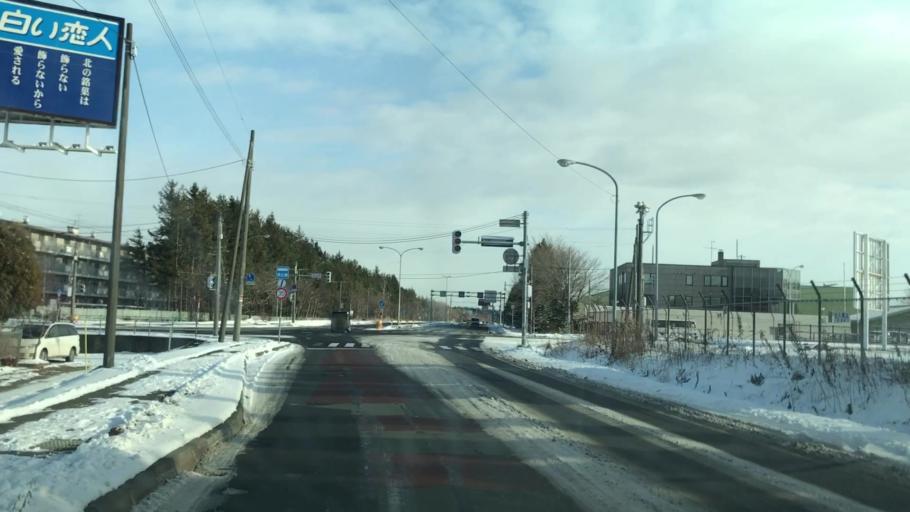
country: JP
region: Hokkaido
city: Chitose
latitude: 42.8147
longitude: 141.6497
